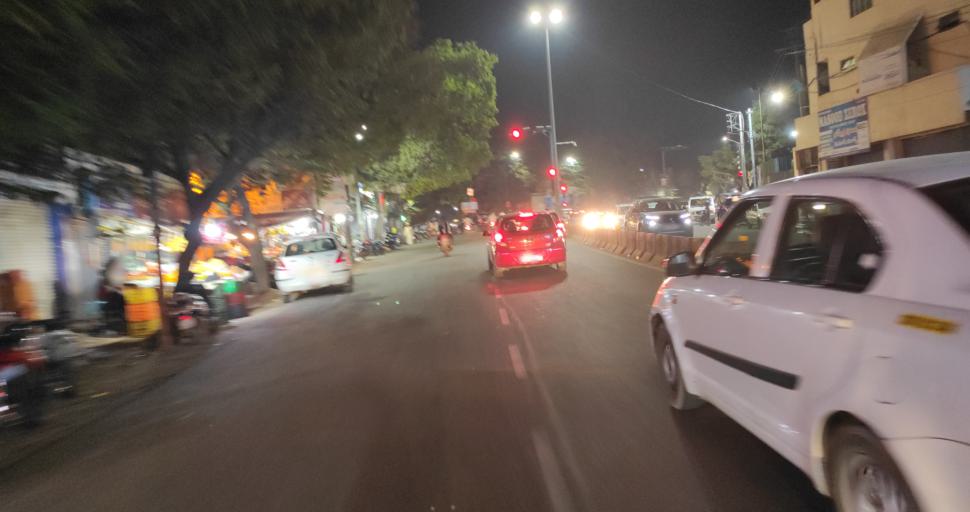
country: IN
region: Telangana
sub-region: Rangareddi
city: Gaddi Annaram
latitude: 17.3634
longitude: 78.5032
